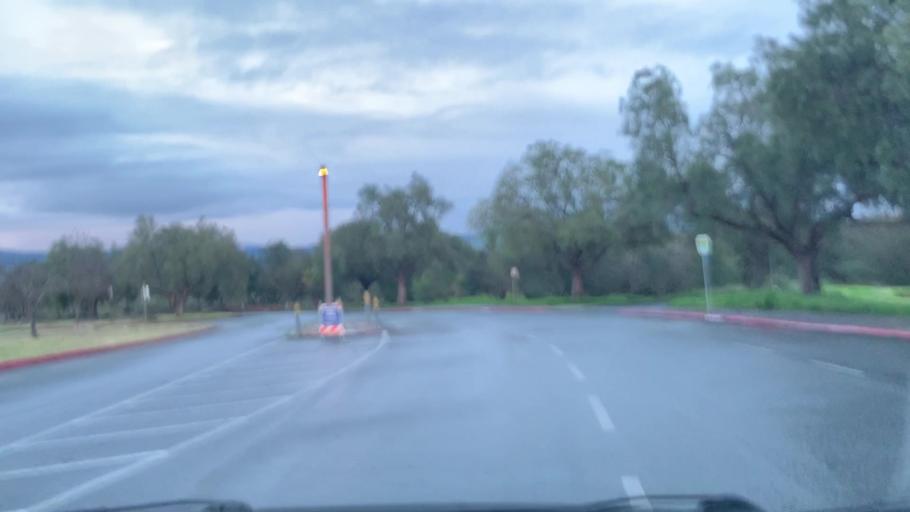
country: US
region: California
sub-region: Santa Clara County
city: Seven Trees
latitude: 37.3199
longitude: -121.8555
